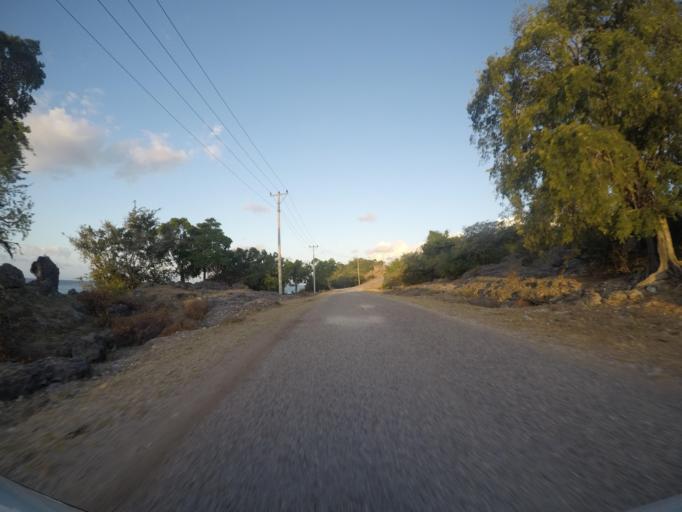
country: TL
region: Lautem
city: Lospalos
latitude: -8.3438
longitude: 127.0430
